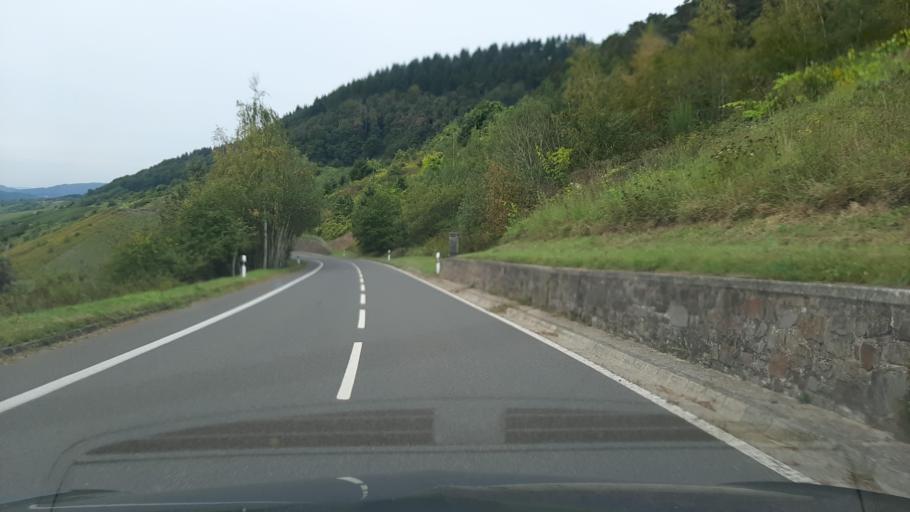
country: DE
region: Rheinland-Pfalz
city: Krov
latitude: 49.9878
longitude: 7.0934
